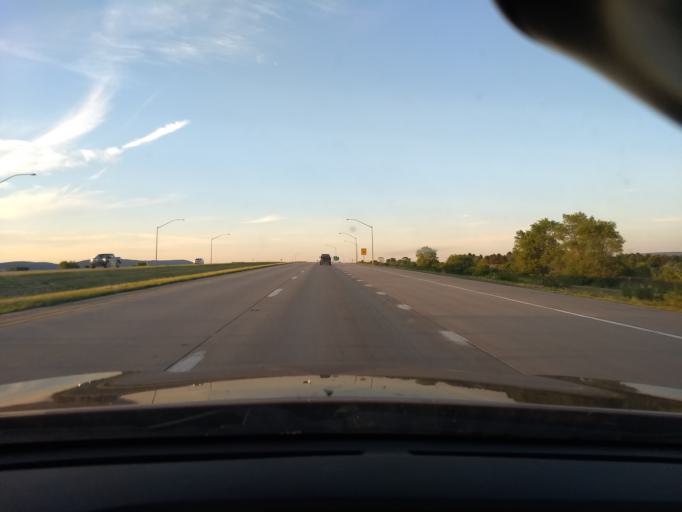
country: US
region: Pennsylvania
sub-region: Centre County
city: Pleasant Gap
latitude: 40.8673
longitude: -77.7841
